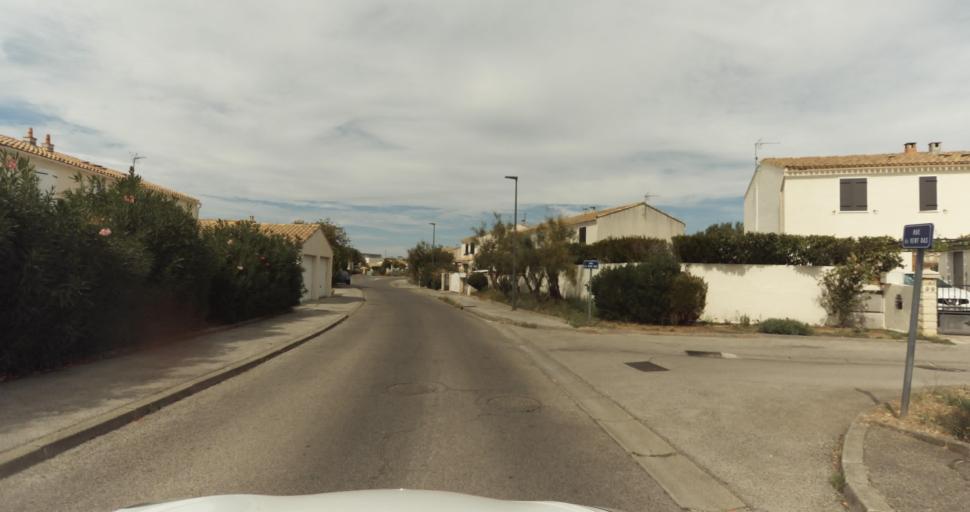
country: FR
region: Provence-Alpes-Cote d'Azur
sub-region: Departement des Bouches-du-Rhone
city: Miramas
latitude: 43.5731
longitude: 4.9979
